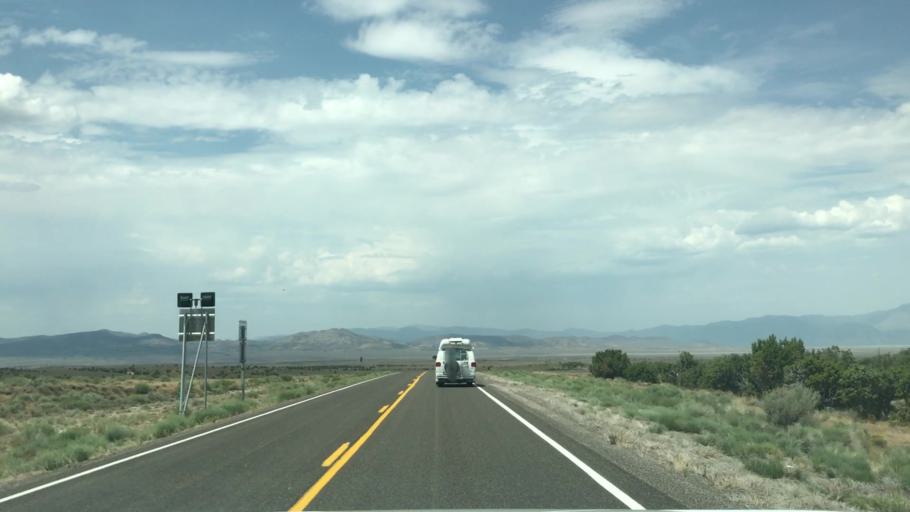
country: US
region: Nevada
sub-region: Eureka County
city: Eureka
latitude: 39.3941
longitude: -115.5243
